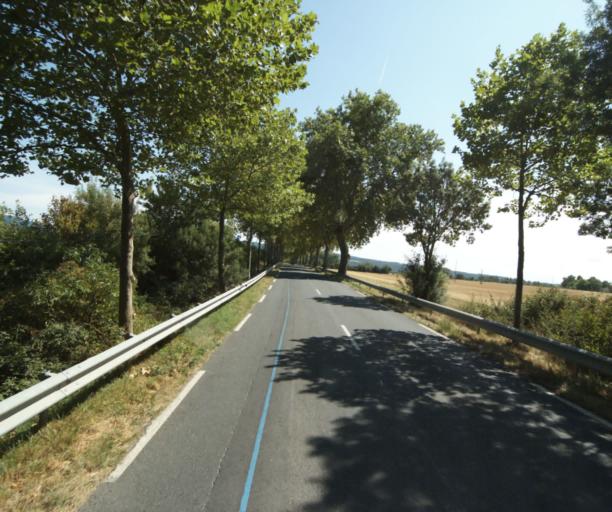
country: FR
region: Midi-Pyrenees
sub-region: Departement de la Haute-Garonne
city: Revel
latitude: 43.4827
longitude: 2.0143
